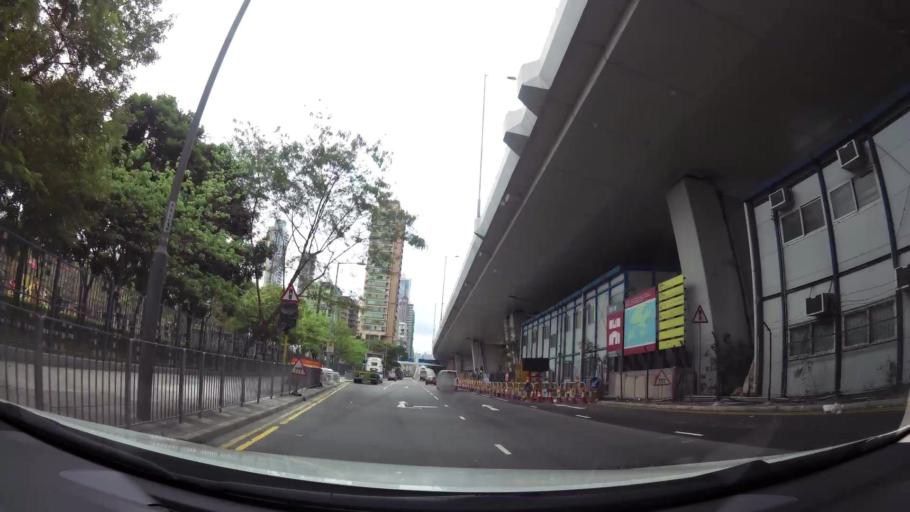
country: HK
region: Sham Shui Po
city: Sham Shui Po
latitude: 22.3303
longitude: 114.1552
